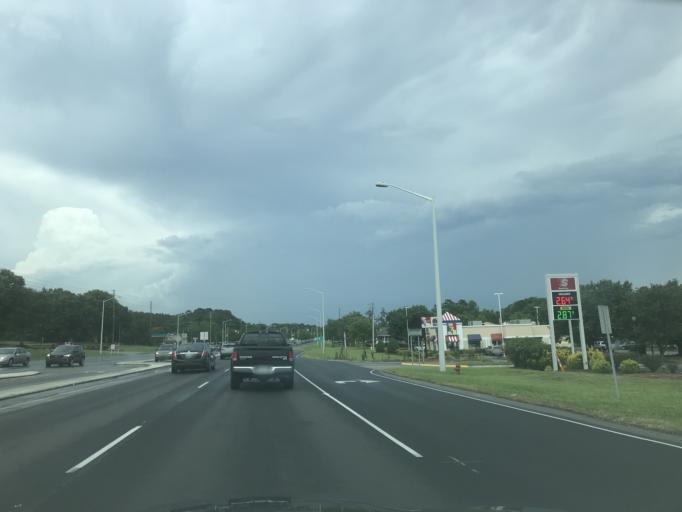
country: US
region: North Carolina
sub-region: Johnston County
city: Clayton
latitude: 35.6551
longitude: -78.4754
